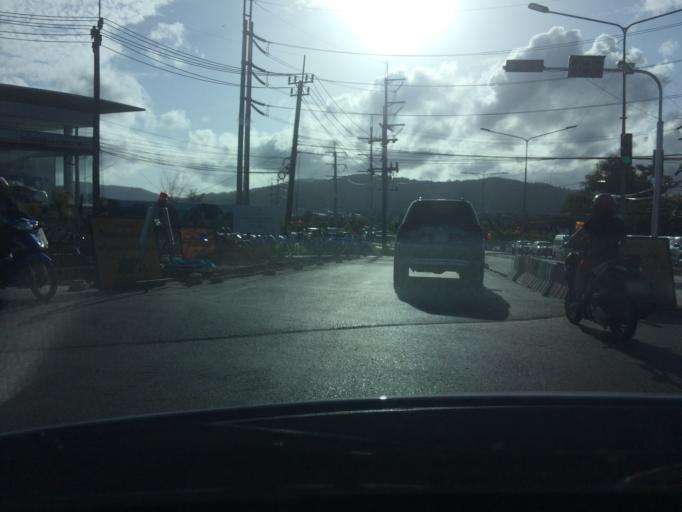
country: TH
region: Phuket
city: Mueang Phuket
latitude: 7.8697
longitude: 98.3750
